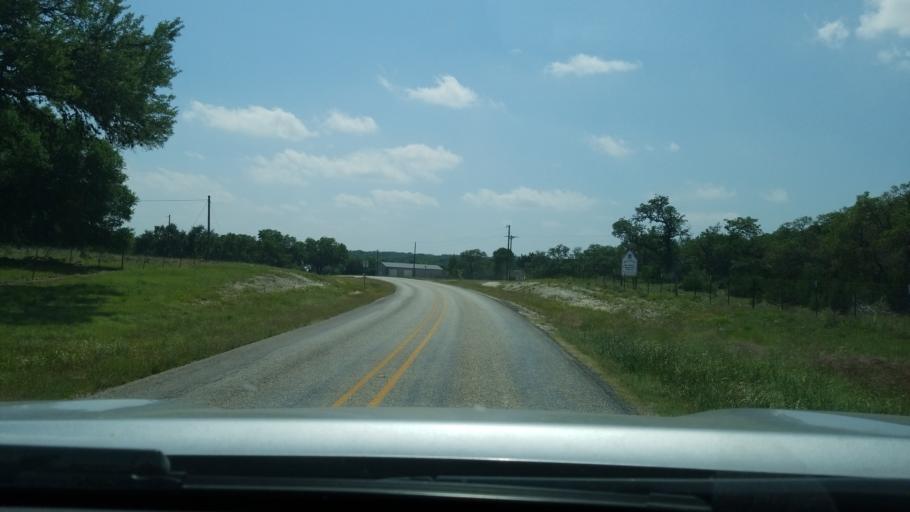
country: US
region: Texas
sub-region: Blanco County
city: Blanco
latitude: 29.9518
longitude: -98.5612
